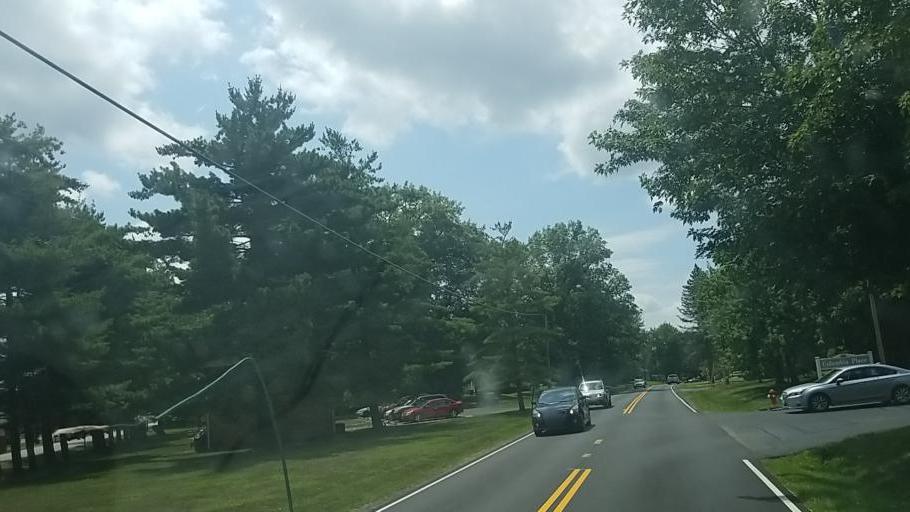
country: US
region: Ohio
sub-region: Fairfield County
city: Pickerington
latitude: 39.8891
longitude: -82.7507
